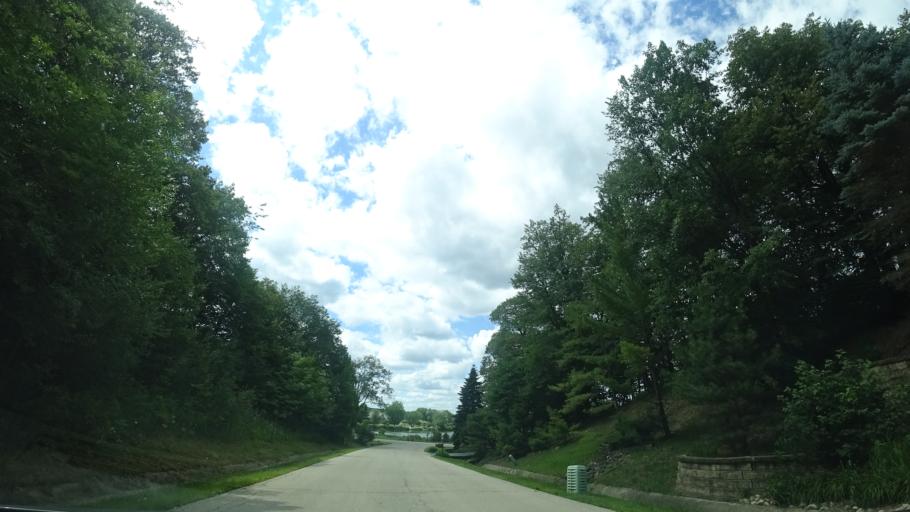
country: US
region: Illinois
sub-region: Will County
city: Homer Glen
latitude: 41.5879
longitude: -87.9169
